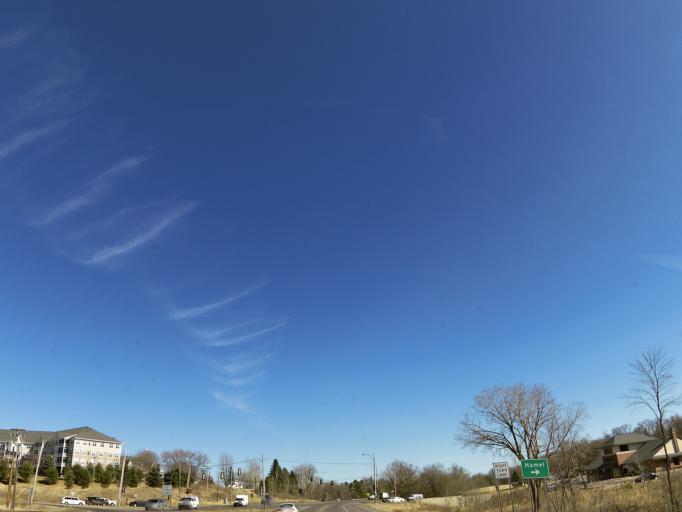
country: US
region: Minnesota
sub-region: Hennepin County
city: Corcoran
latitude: 45.0436
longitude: -93.5273
